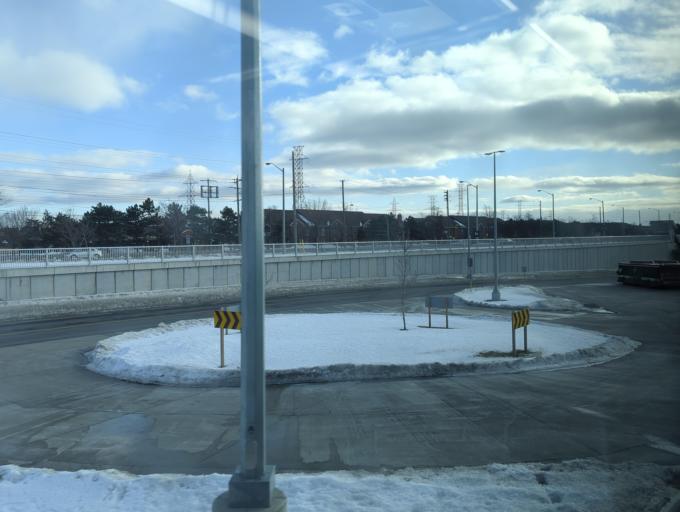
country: CA
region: Ontario
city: Etobicoke
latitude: 43.6653
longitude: -79.5891
